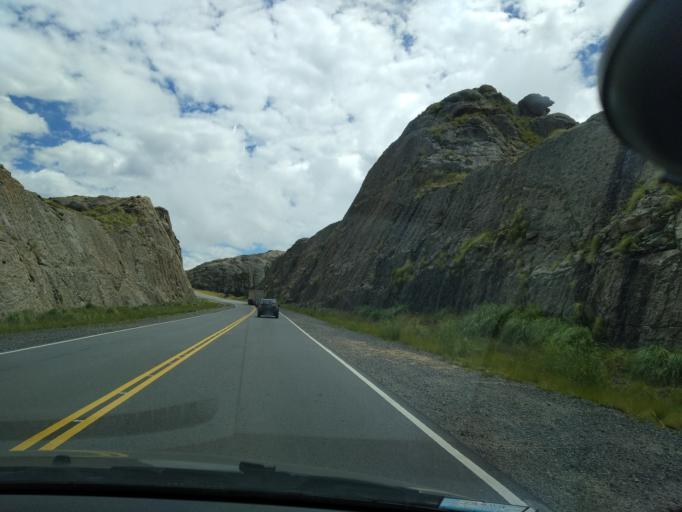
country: AR
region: Cordoba
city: Mina Clavero
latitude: -31.6683
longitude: -64.9001
